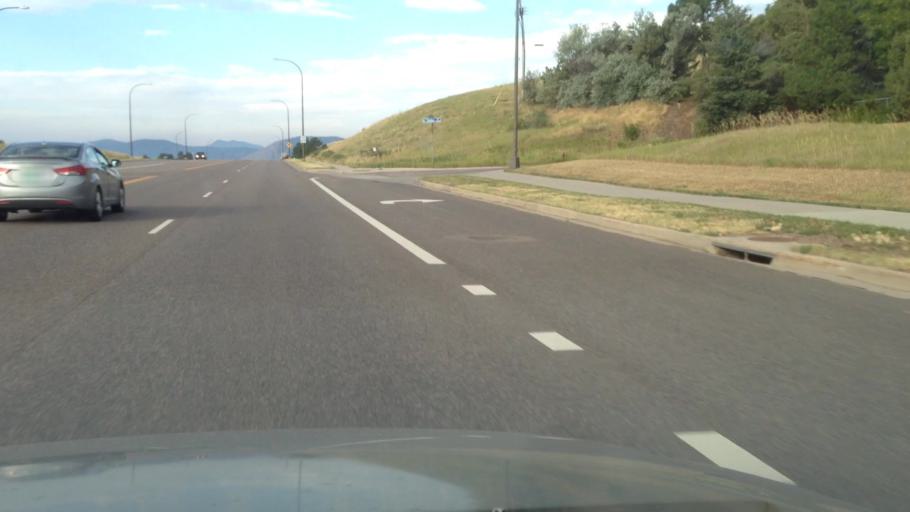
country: US
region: Colorado
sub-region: Jefferson County
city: West Pleasant View
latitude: 39.6924
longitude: -105.1496
